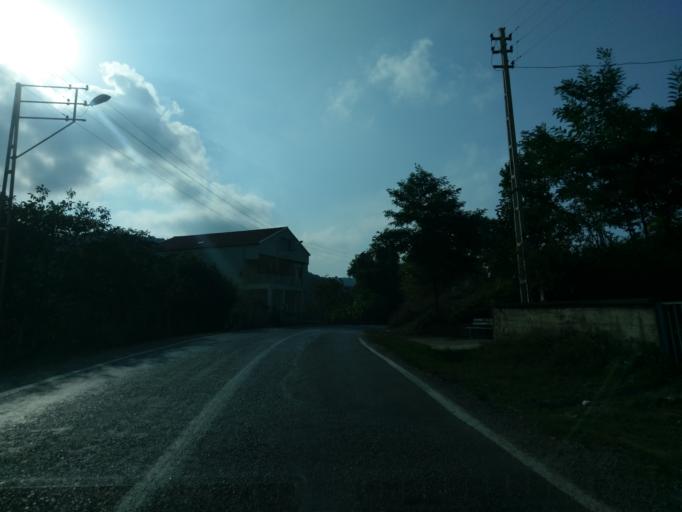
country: TR
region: Sinop
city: Helaldi
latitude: 41.9367
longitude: 34.4062
